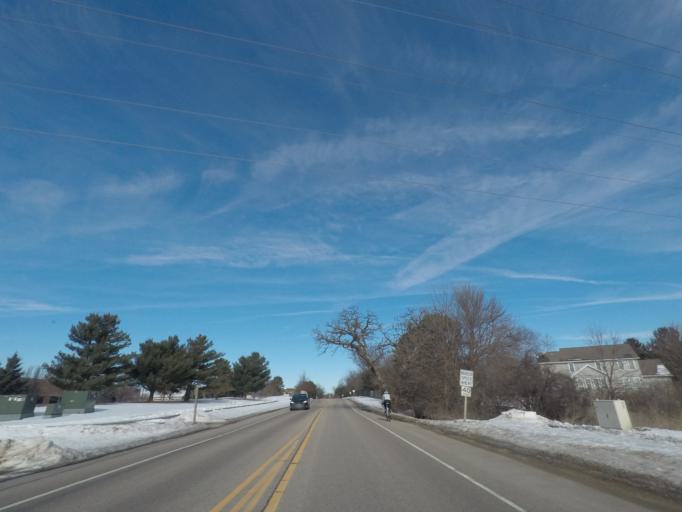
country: US
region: Wisconsin
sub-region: Dane County
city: Fitchburg
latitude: 43.0081
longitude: -89.4574
